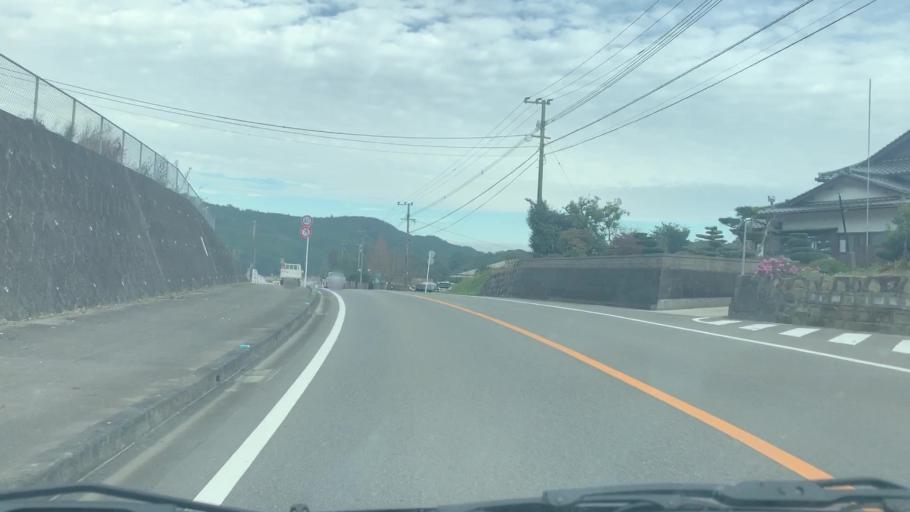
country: JP
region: Saga Prefecture
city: Takeocho-takeo
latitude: 33.2443
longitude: 129.9700
